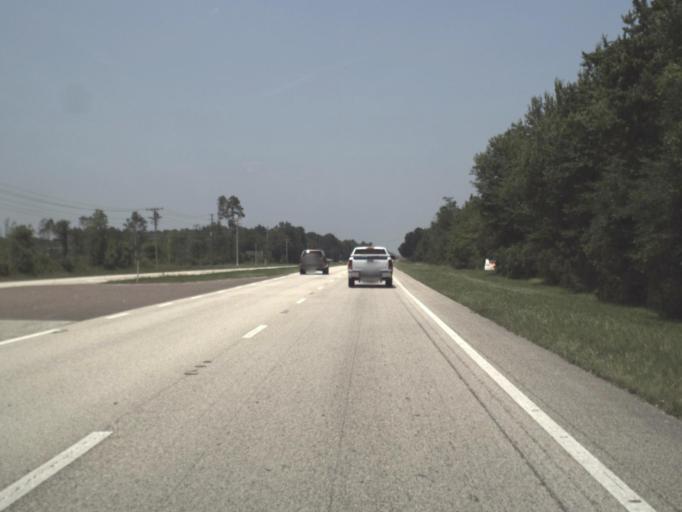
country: US
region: Florida
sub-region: Duval County
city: Baldwin
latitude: 30.1801
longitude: -82.0228
